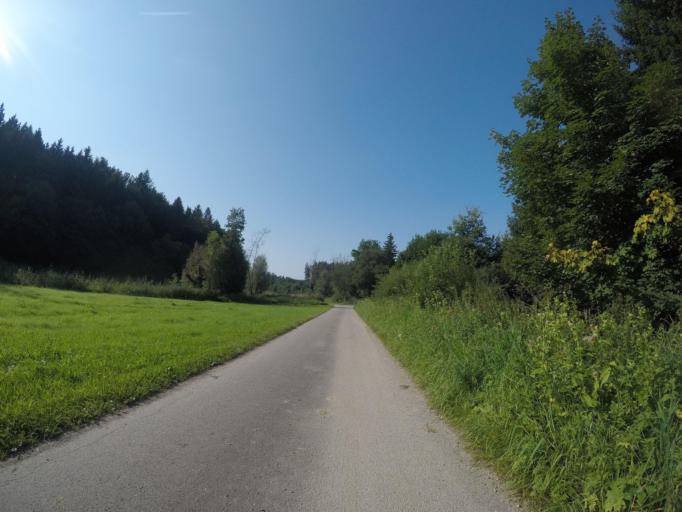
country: DE
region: Baden-Wuerttemberg
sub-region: Tuebingen Region
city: Schnurpflingen
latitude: 48.2547
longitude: 10.0072
